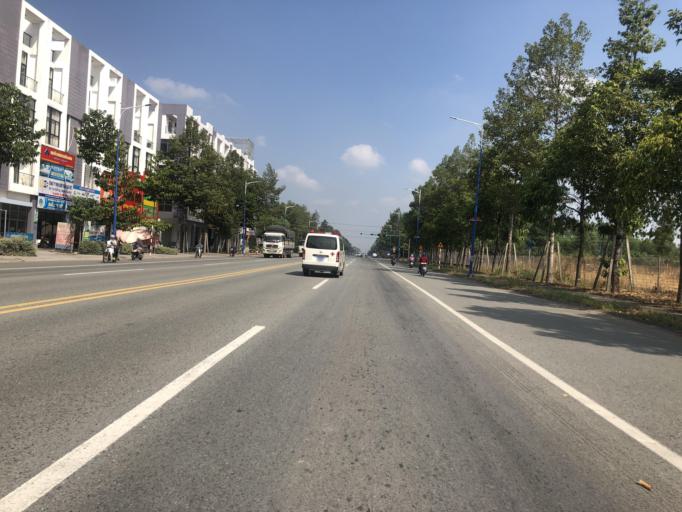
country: VN
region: Binh Duong
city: Thu Dau Mot
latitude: 11.0698
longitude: 106.6764
